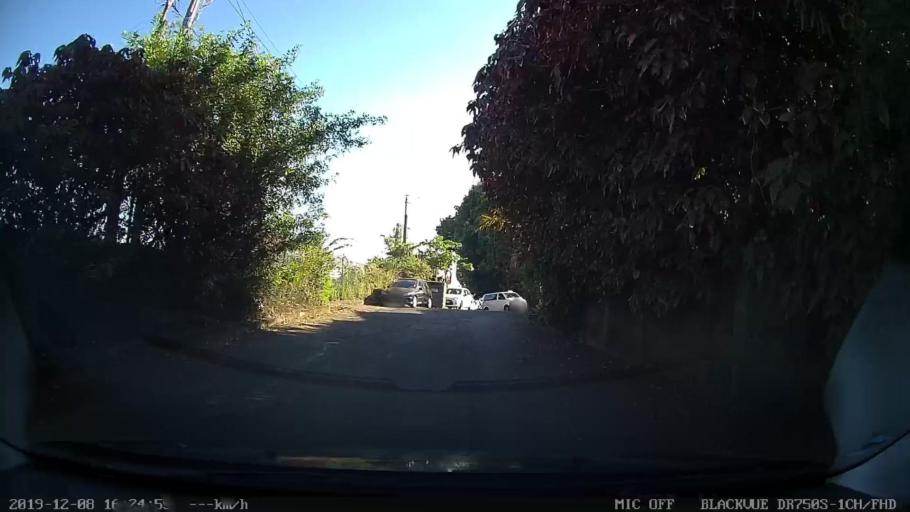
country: RE
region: Reunion
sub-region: Reunion
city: Sainte-Marie
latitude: -20.9245
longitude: 55.5317
